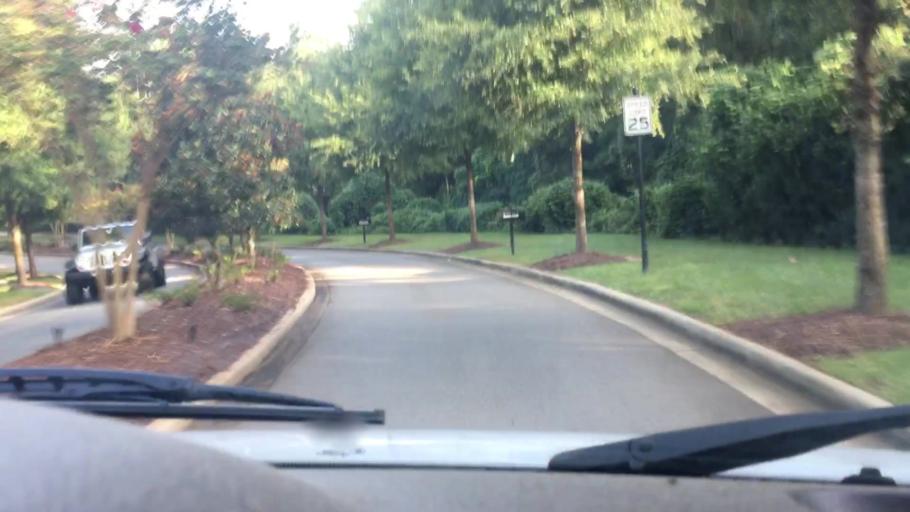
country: US
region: North Carolina
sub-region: Mecklenburg County
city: Huntersville
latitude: 35.4108
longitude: -80.8379
